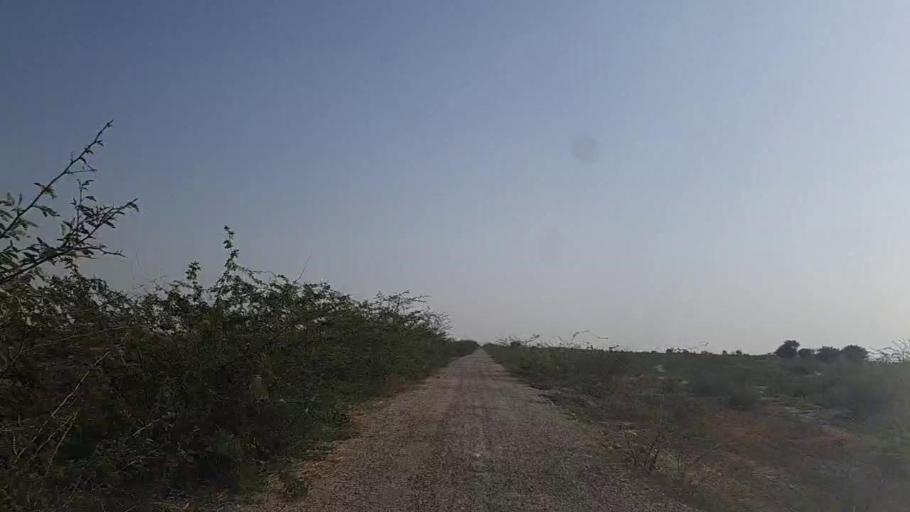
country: PK
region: Sindh
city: Kadhan
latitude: 24.5923
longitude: 69.2627
